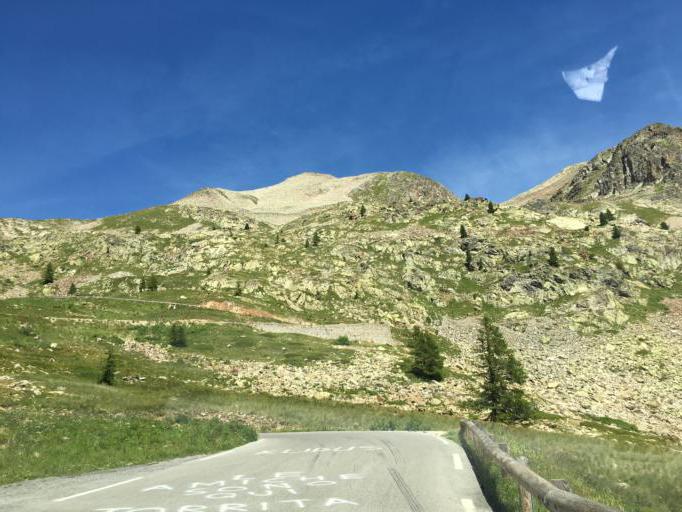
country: IT
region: Piedmont
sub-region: Provincia di Cuneo
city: Vinadio
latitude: 44.1990
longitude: 7.1552
